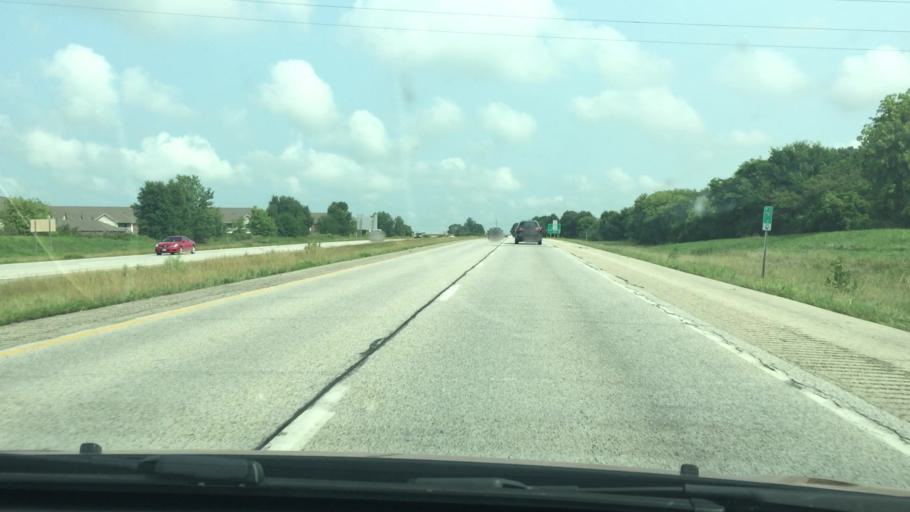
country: US
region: Iowa
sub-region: Scott County
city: Bettendorf
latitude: 41.5818
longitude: -90.5219
